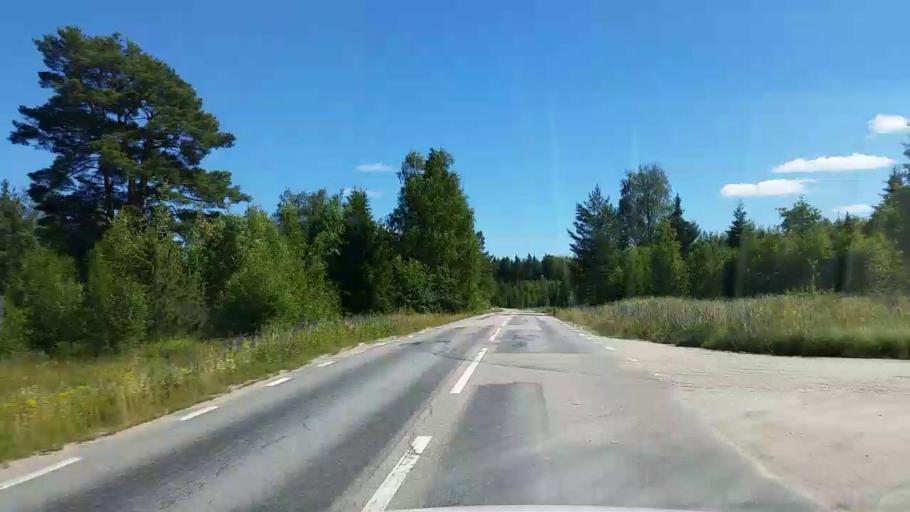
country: SE
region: Gaevleborg
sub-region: Ovanakers Kommun
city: Edsbyn
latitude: 61.3303
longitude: 15.8360
